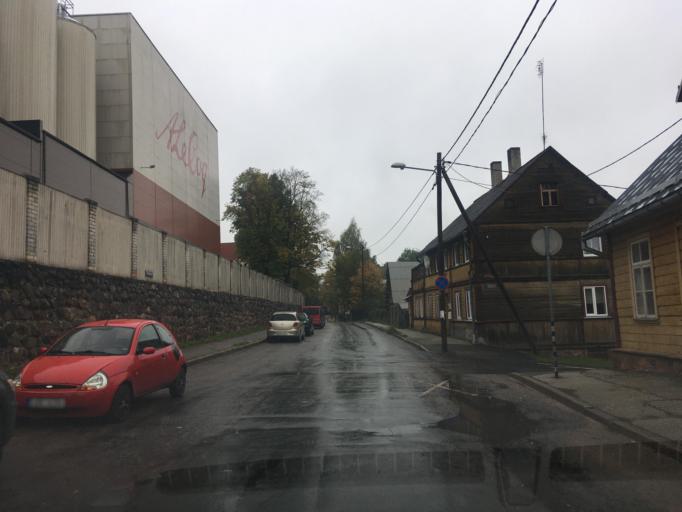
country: EE
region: Tartu
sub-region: Tartu linn
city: Tartu
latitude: 58.3862
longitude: 26.7083
